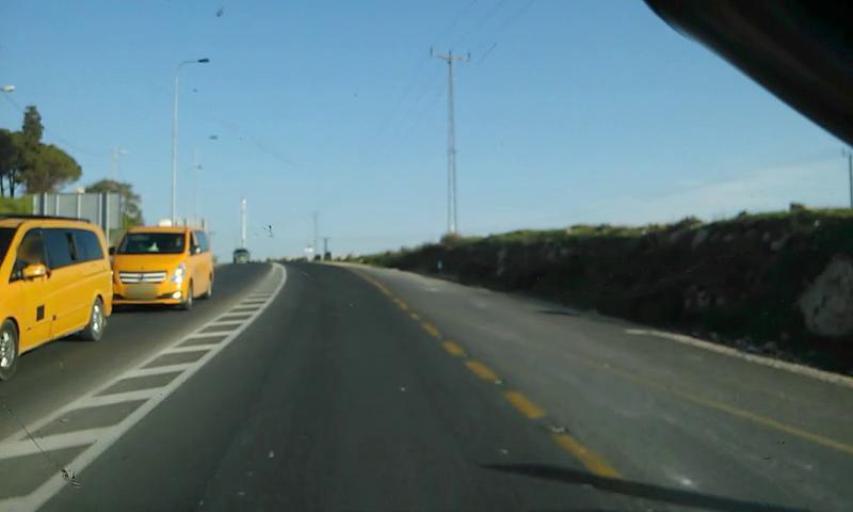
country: PS
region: West Bank
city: Jurat ash Sham`ah
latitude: 31.6477
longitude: 35.1484
